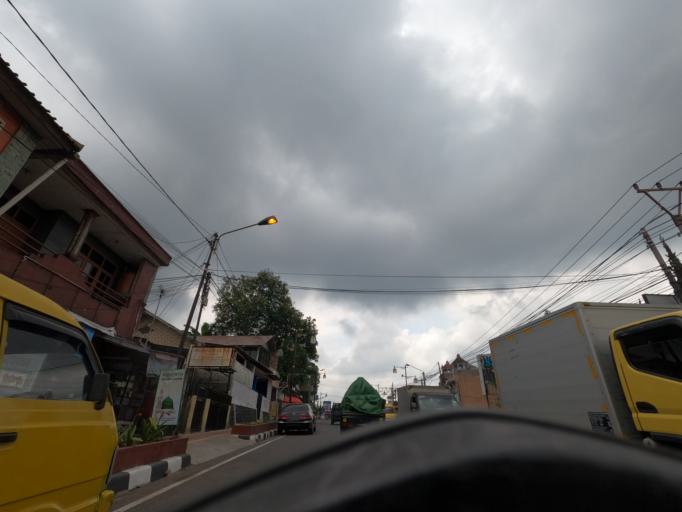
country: ID
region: West Java
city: Sukabumi
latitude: -6.7454
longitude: 107.0475
